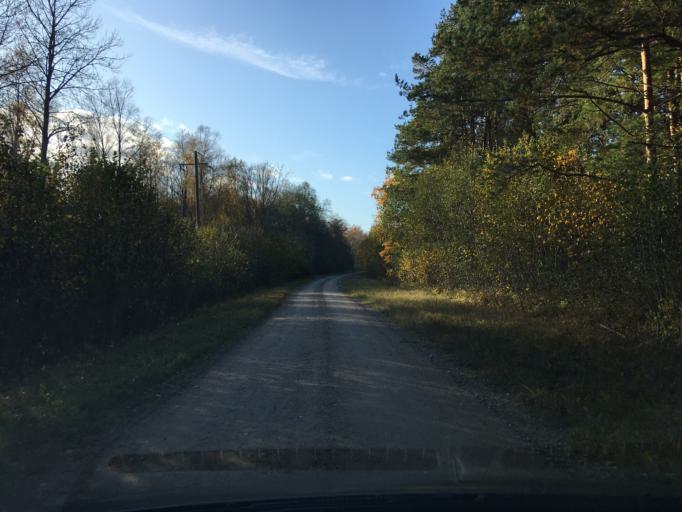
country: EE
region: Laeaene
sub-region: Lihula vald
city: Lihula
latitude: 58.5680
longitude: 23.7589
